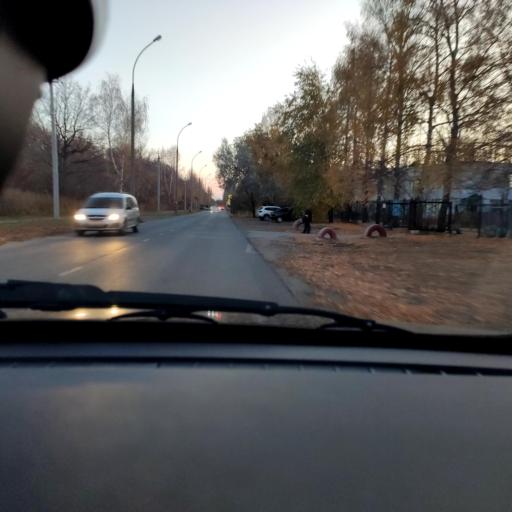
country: RU
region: Samara
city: Tol'yatti
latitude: 53.5083
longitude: 49.3072
